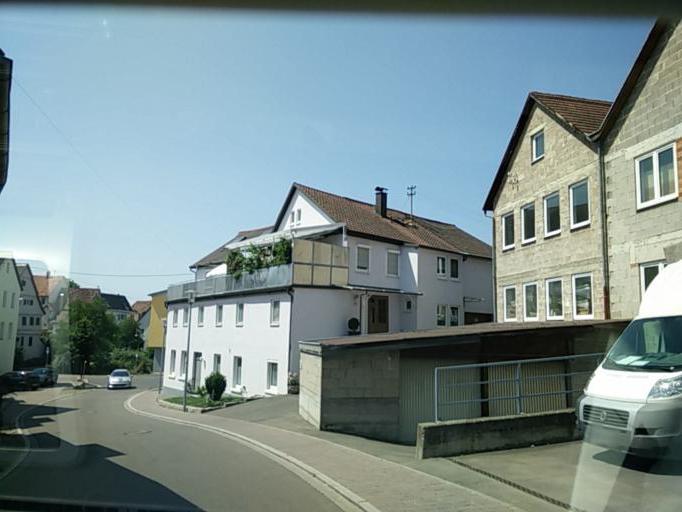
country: DE
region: Baden-Wuerttemberg
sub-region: Tuebingen Region
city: Gomaringen
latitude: 48.4542
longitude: 9.1007
